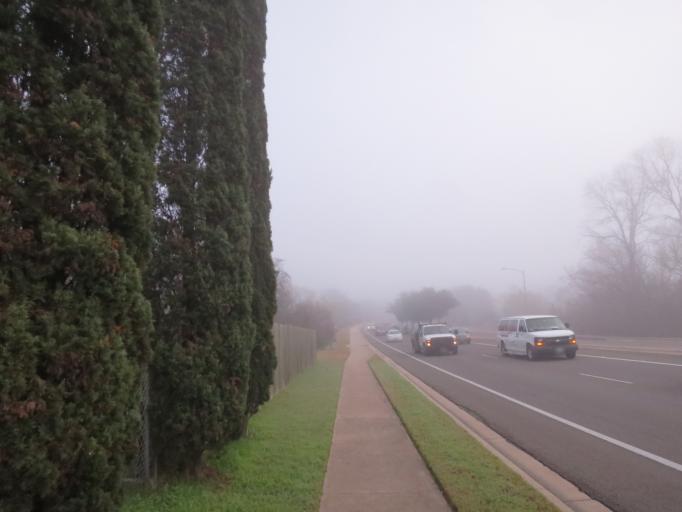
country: US
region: Texas
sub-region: Travis County
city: Wells Branch
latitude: 30.4205
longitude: -97.6838
